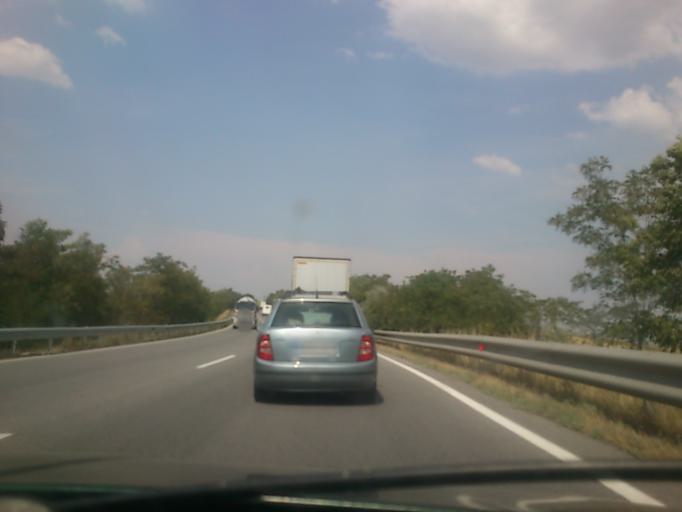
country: AT
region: Lower Austria
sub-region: Politischer Bezirk Mistelbach
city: Drasenhofen
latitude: 48.7293
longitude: 16.6579
